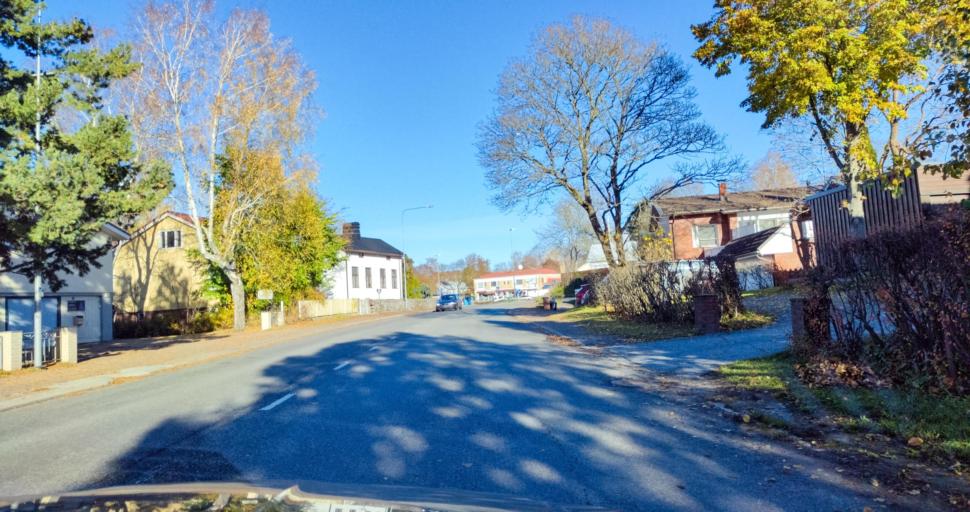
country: FI
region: Varsinais-Suomi
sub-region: Turku
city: Turku
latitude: 60.4339
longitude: 22.2586
